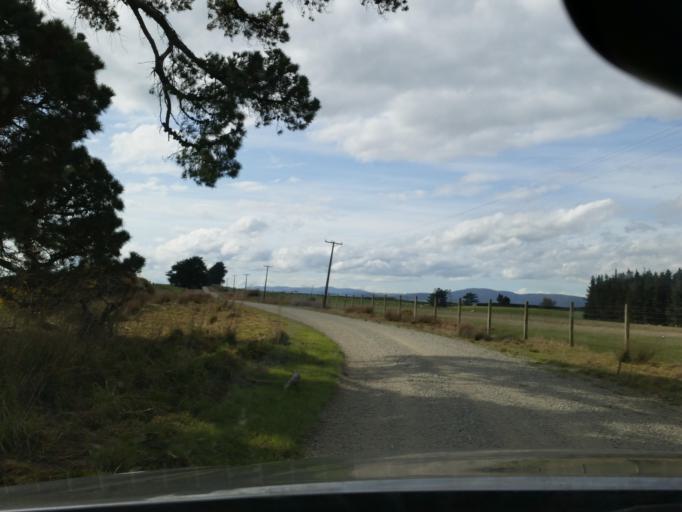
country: NZ
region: Southland
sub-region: Southland District
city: Winton
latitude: -46.2132
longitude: 168.4851
